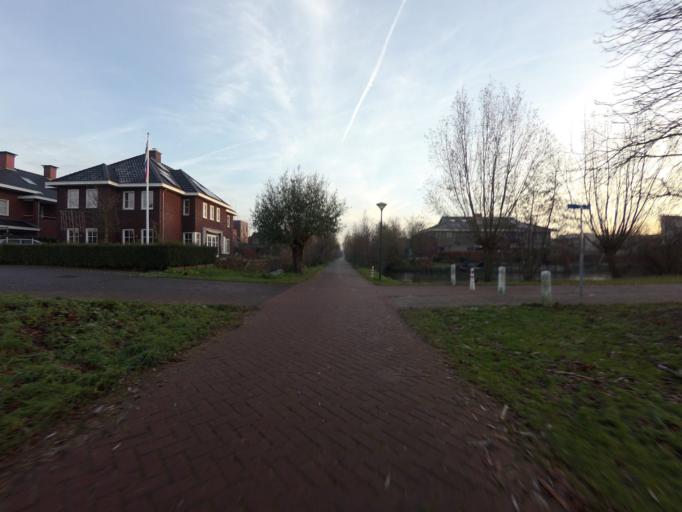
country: NL
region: Utrecht
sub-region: Gemeente Woerden
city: Woerden
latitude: 52.0867
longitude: 4.9078
